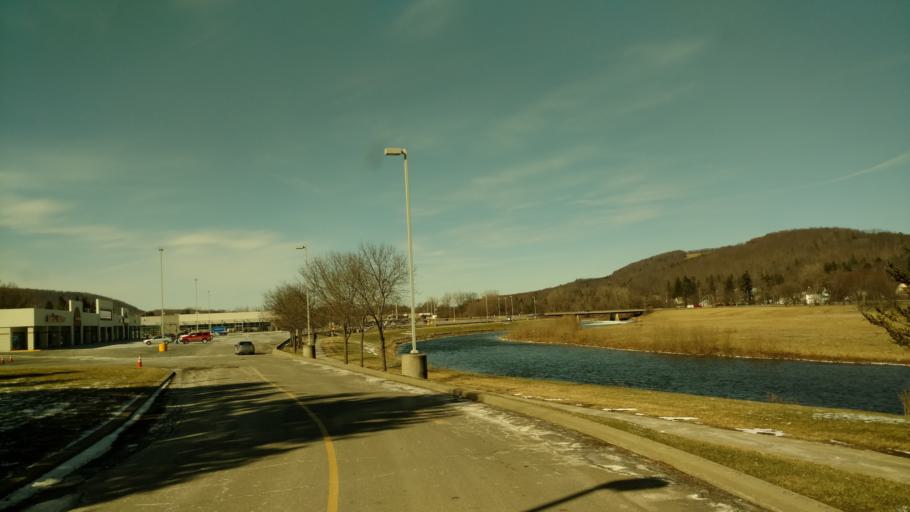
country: US
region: New York
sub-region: Allegany County
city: Wellsville
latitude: 42.1237
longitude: -77.9604
